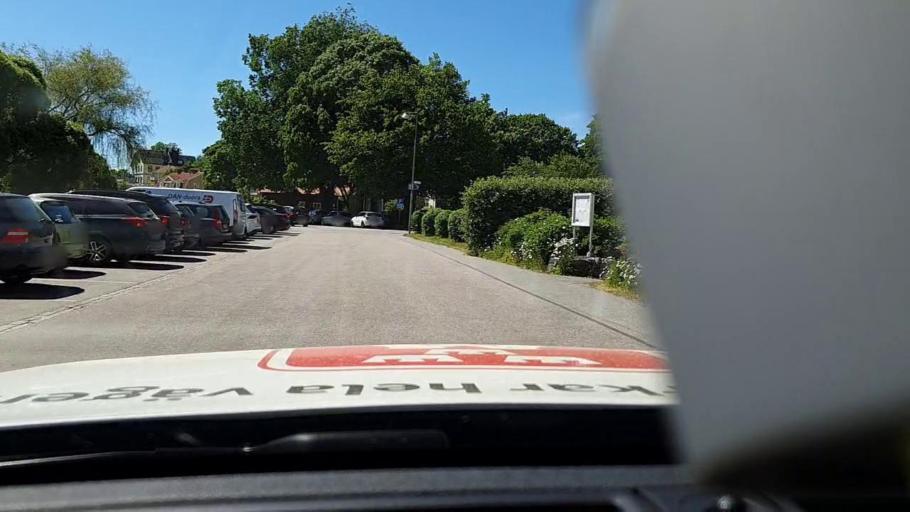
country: SE
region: Stockholm
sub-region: Sigtuna Kommun
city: Sigtuna
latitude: 59.6161
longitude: 17.7239
